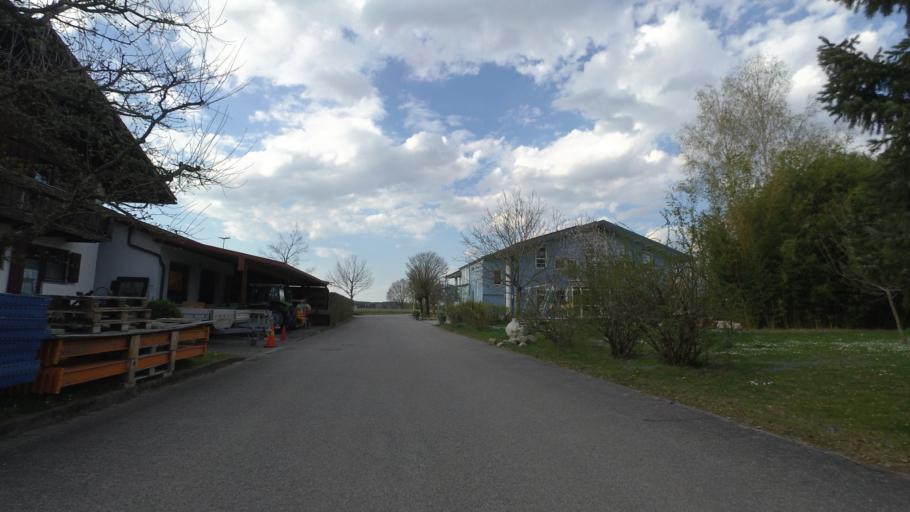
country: DE
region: Bavaria
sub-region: Upper Bavaria
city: Seeon-Seebruck
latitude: 47.9405
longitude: 12.4799
